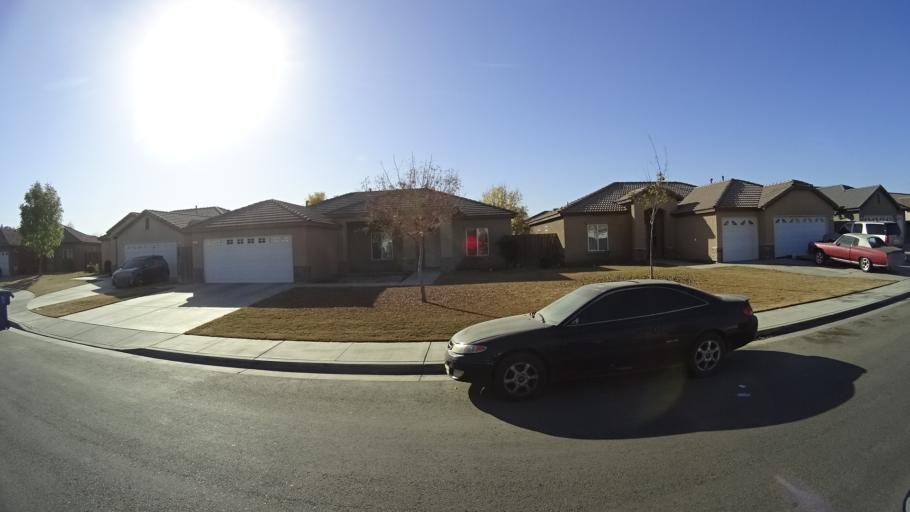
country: US
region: California
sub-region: Kern County
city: Greenfield
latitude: 35.2707
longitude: -119.0400
